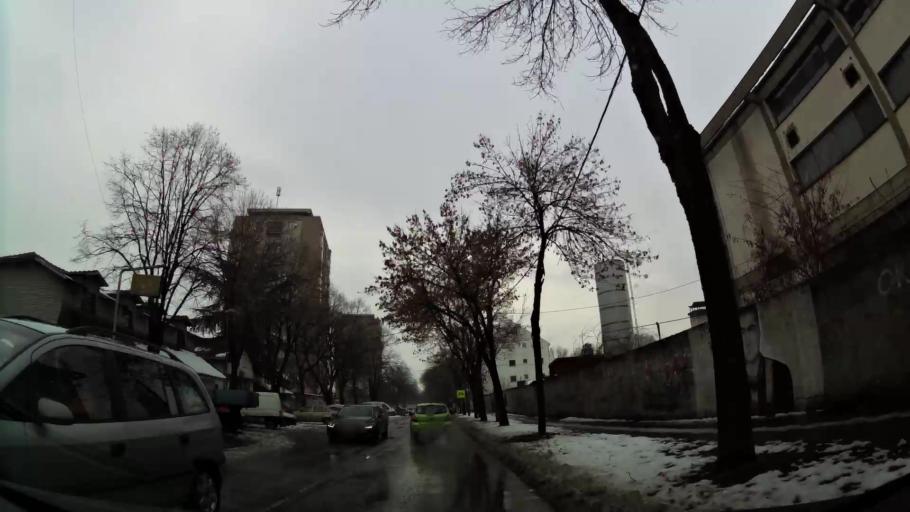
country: RS
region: Central Serbia
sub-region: Belgrade
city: Zemun
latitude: 44.8388
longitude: 20.3930
